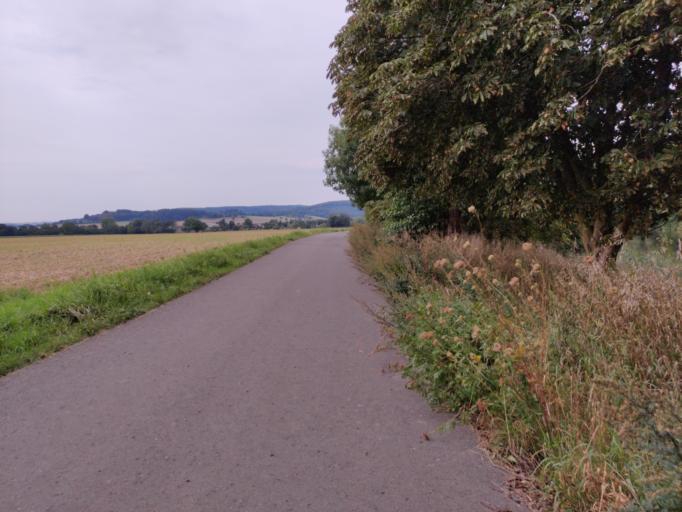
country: DE
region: Lower Saxony
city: Hameln
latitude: 52.0713
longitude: 9.3601
